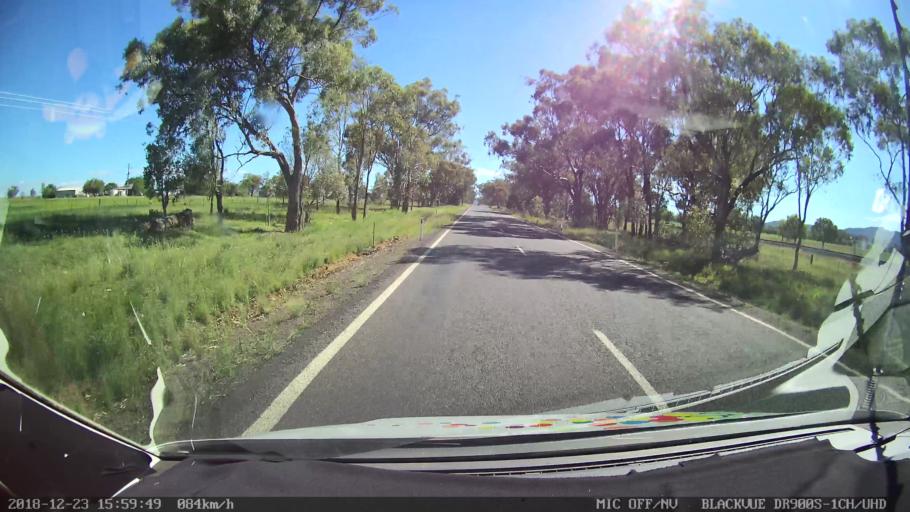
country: AU
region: New South Wales
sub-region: Tamworth Municipality
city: Phillip
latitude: -31.2039
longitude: 150.8301
